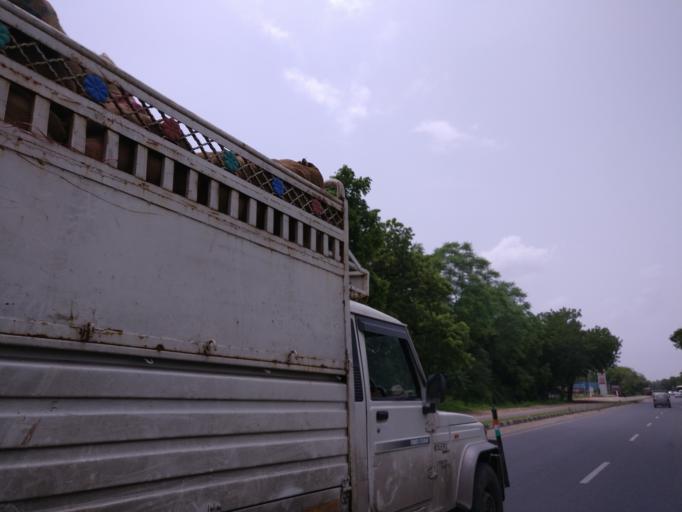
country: IN
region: Gujarat
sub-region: Mahesana
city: Jhulasan
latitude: 23.2567
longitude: 72.4796
